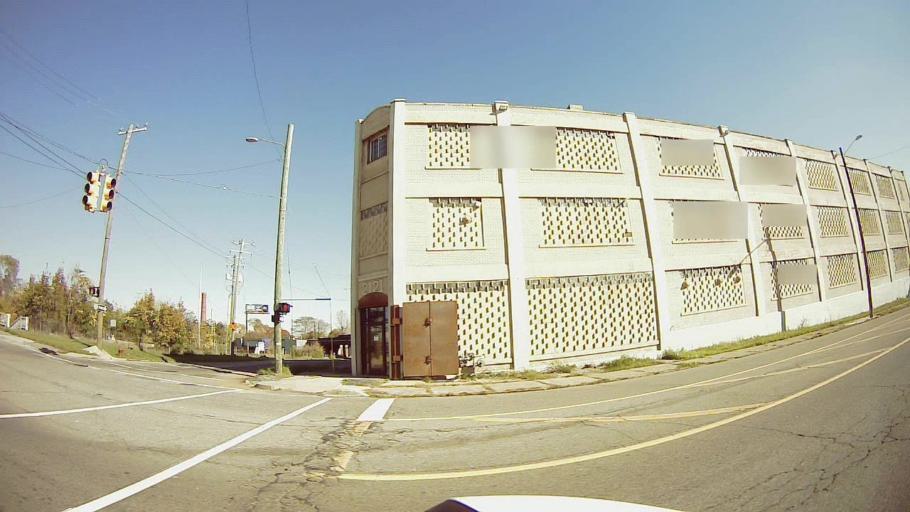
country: US
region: Michigan
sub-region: Wayne County
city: Detroit
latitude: 42.3529
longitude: -83.0889
